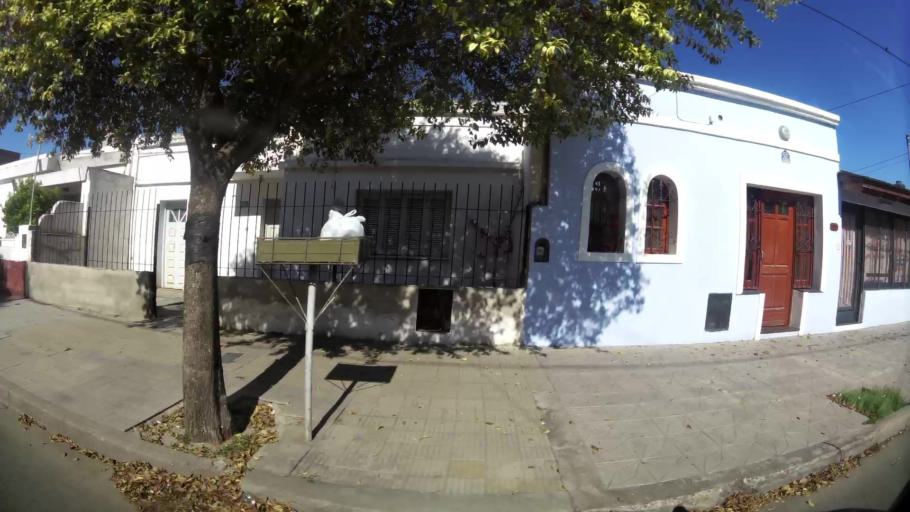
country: AR
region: Cordoba
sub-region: Departamento de Capital
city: Cordoba
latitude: -31.3905
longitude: -64.1341
